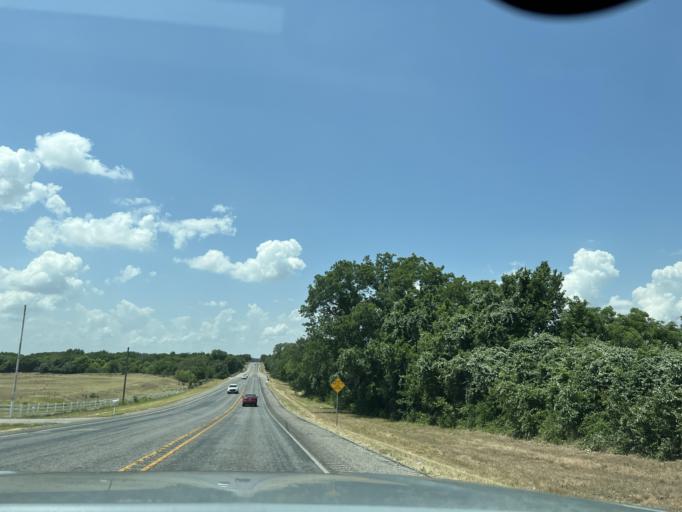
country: US
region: Texas
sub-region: Parker County
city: Springtown
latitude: 32.8741
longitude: -97.7425
